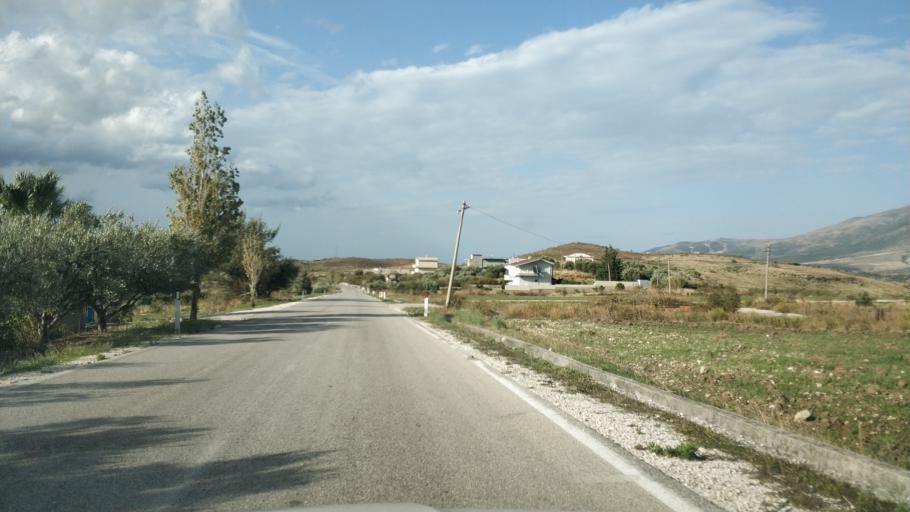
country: AL
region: Vlore
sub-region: Rrethi i Vlores
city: Orikum
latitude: 40.3067
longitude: 19.4819
